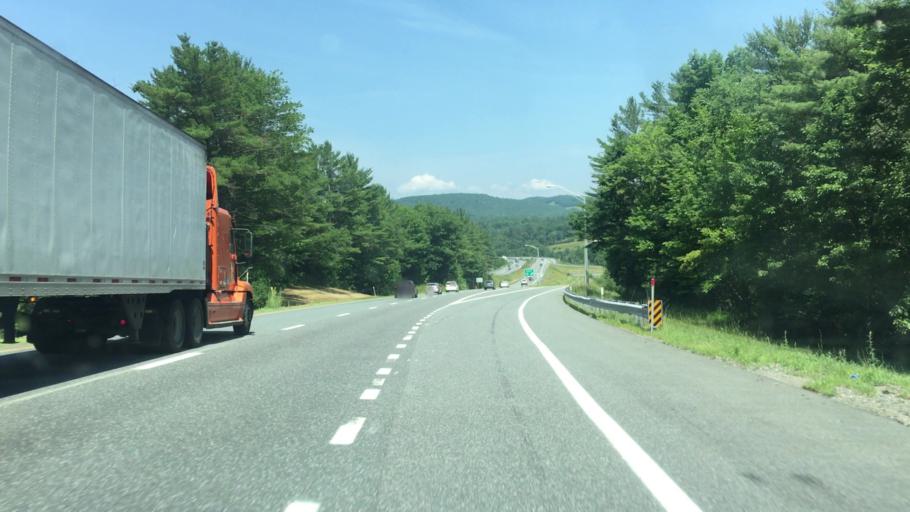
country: US
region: New Hampshire
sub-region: Grafton County
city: Lebanon
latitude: 43.6296
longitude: -72.2093
